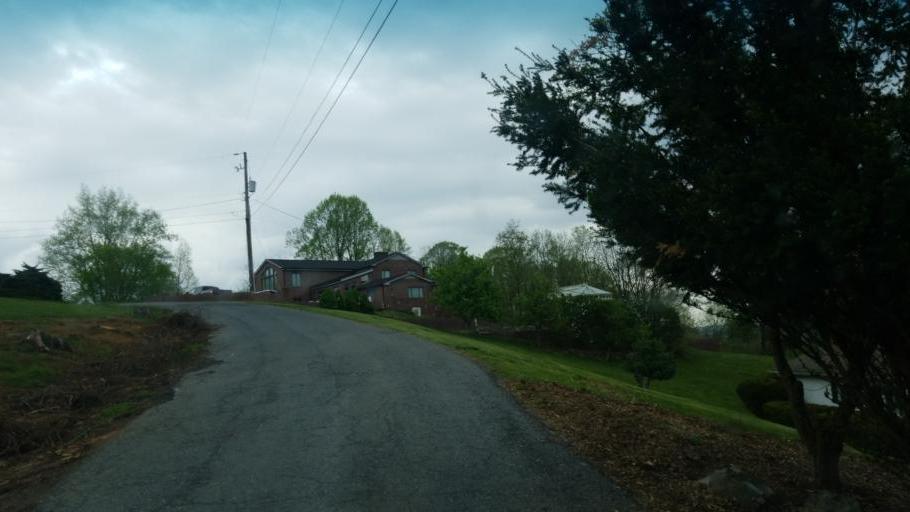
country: US
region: Virginia
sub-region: Smyth County
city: Marion
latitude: 36.8521
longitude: -81.4923
